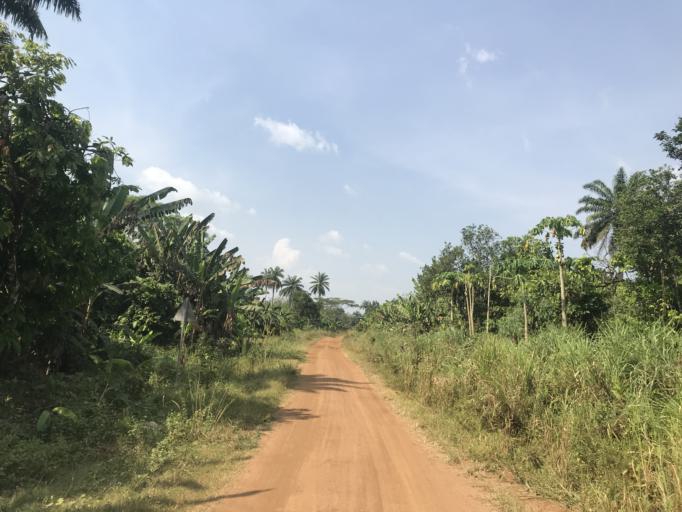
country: NG
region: Osun
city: Osu
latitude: 7.6421
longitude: 4.6585
